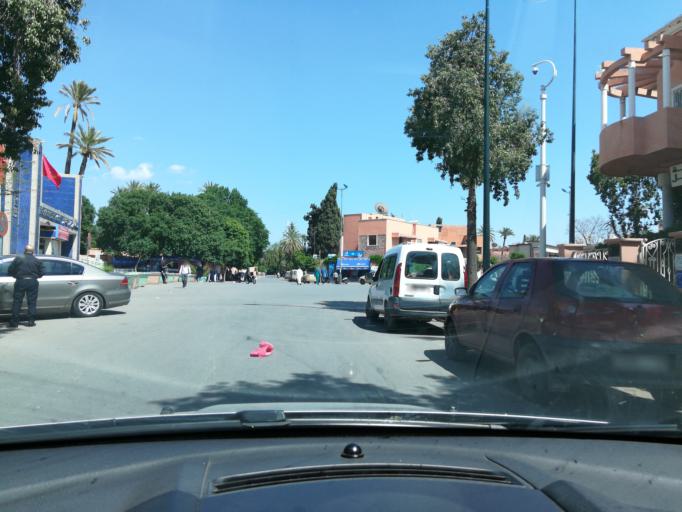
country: MA
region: Marrakech-Tensift-Al Haouz
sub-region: Marrakech
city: Marrakesh
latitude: 31.6407
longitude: -8.0157
